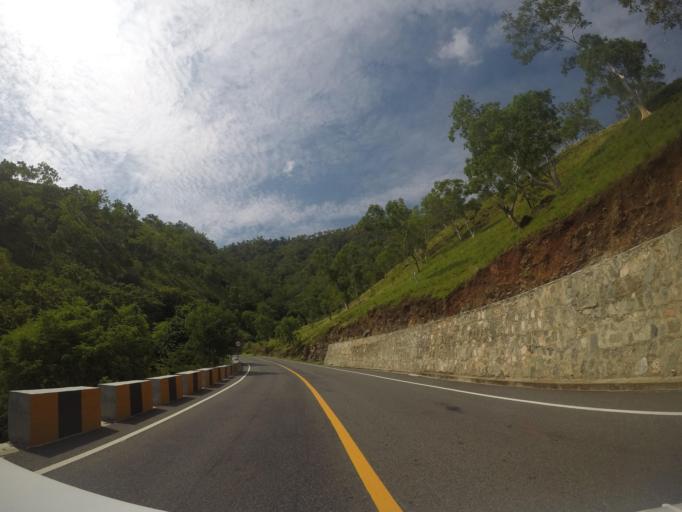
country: TL
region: Manatuto
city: Manatuto
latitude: -8.4850
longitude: 125.9458
